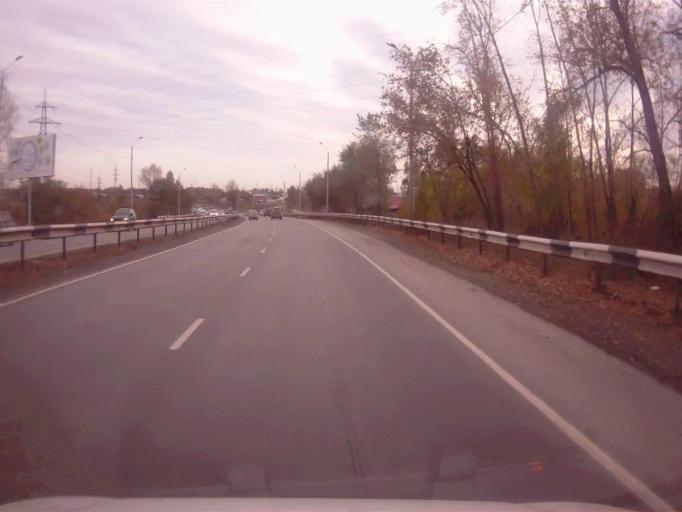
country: RU
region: Chelyabinsk
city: Novosineglazovskiy
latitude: 55.0486
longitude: 61.4149
